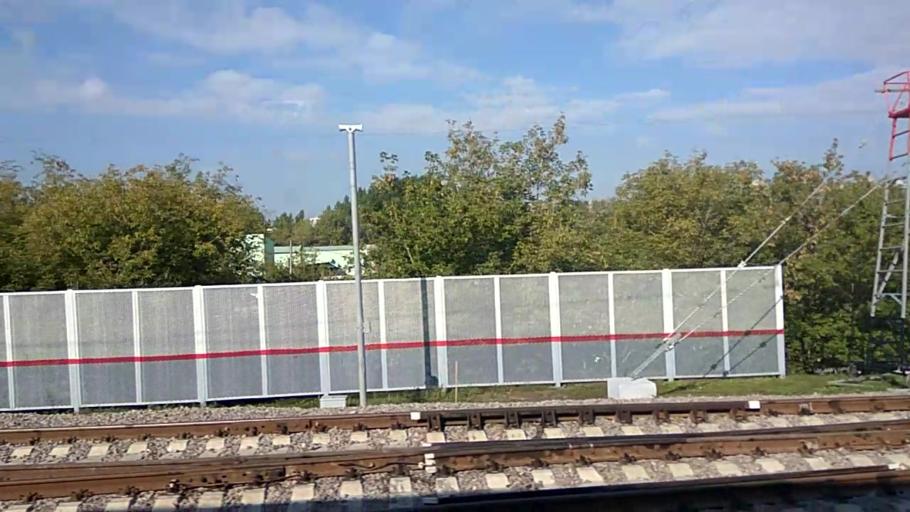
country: RU
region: Moscow
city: Ryazanskiy
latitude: 55.7357
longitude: 37.7305
